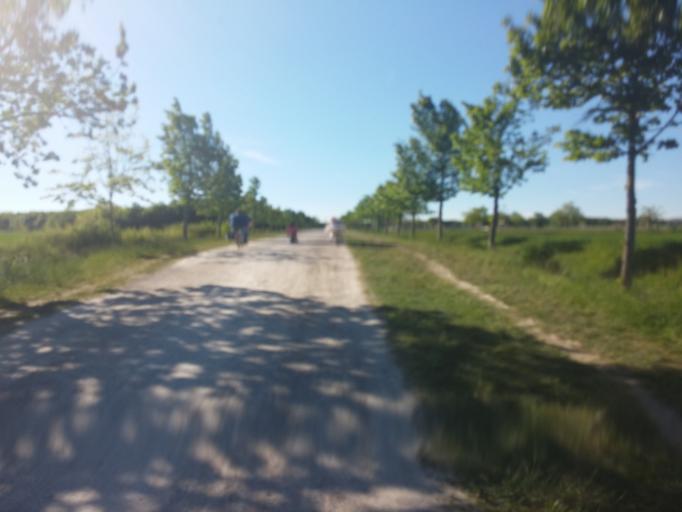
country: DE
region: Bavaria
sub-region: Upper Bavaria
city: Haar
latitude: 48.1231
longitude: 11.7061
